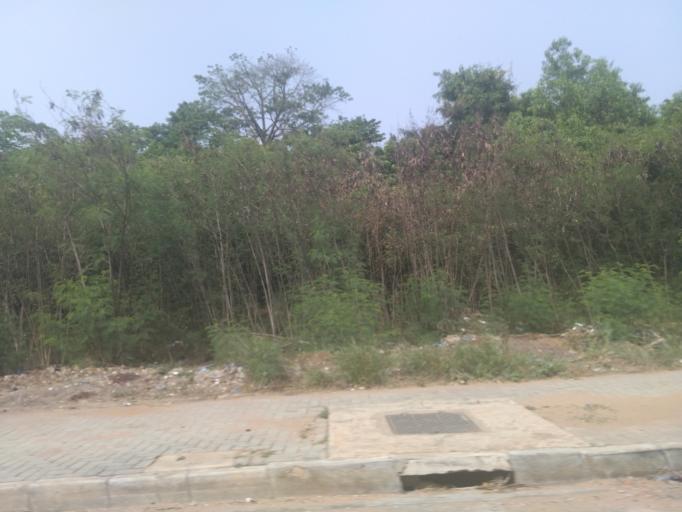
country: GH
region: Greater Accra
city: Dome
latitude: 5.6167
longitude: -0.2016
